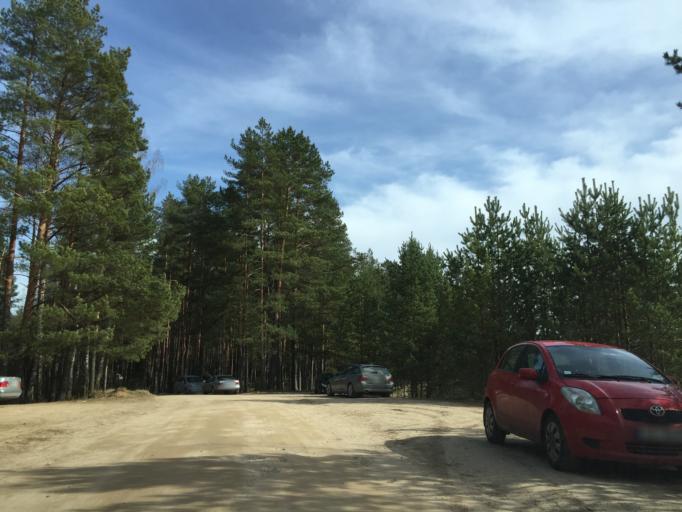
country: LV
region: Ikskile
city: Ikskile
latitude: 56.8411
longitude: 24.5528
